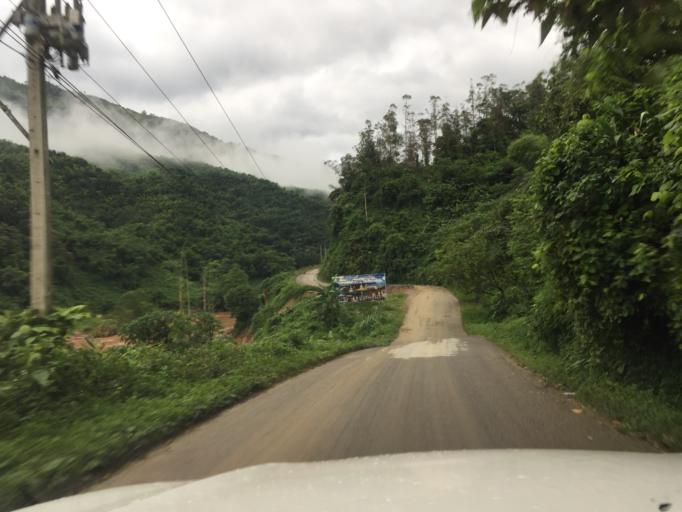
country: LA
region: Oudomxai
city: Muang La
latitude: 21.0029
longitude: 102.2324
